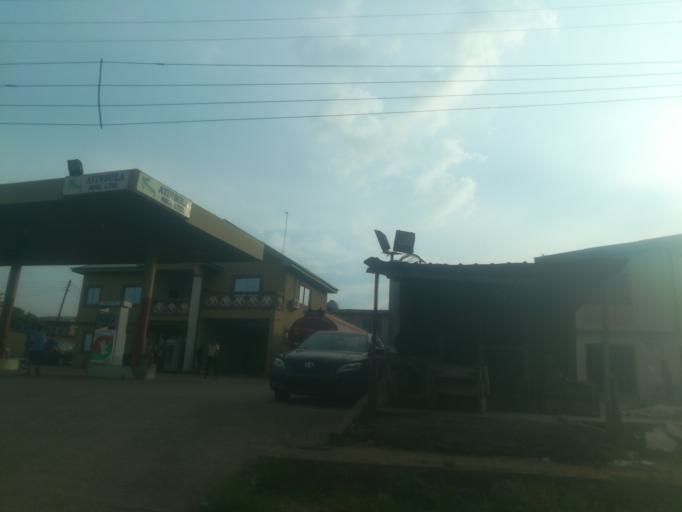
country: NG
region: Ogun
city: Abeokuta
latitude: 7.1637
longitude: 3.3125
